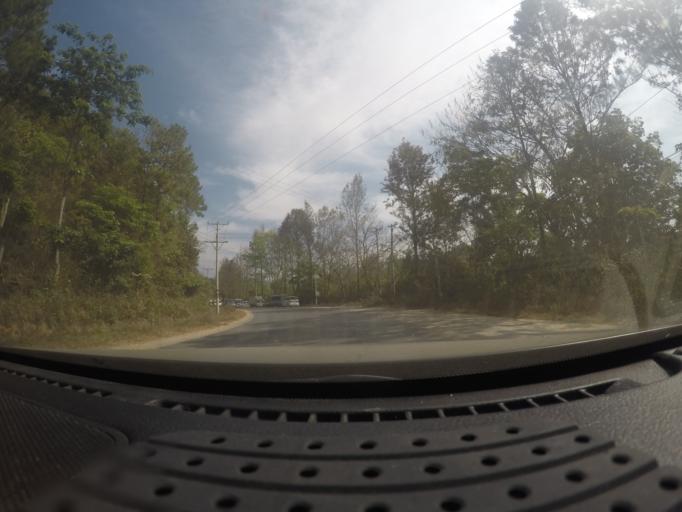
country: MM
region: Shan
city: Taunggyi
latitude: 20.6330
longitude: 96.5856
